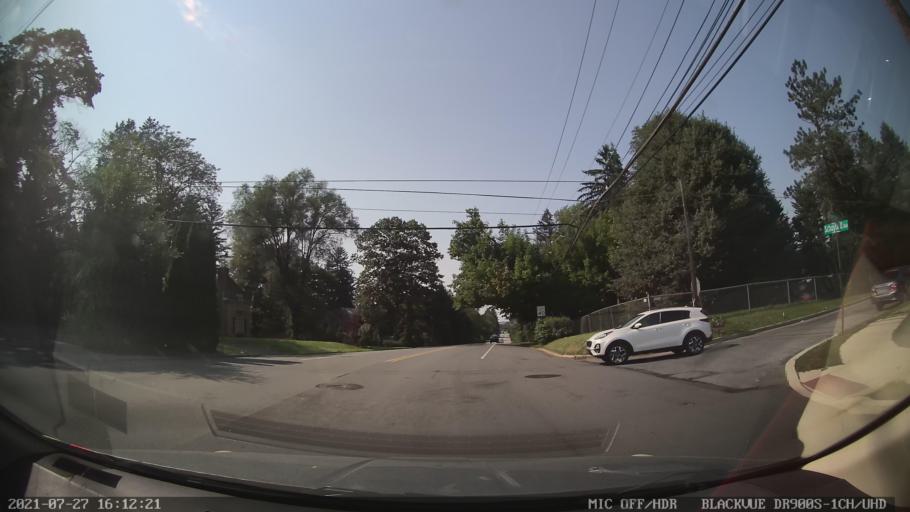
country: US
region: Pennsylvania
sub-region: Berks County
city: West Reading
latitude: 40.3586
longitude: -75.9511
